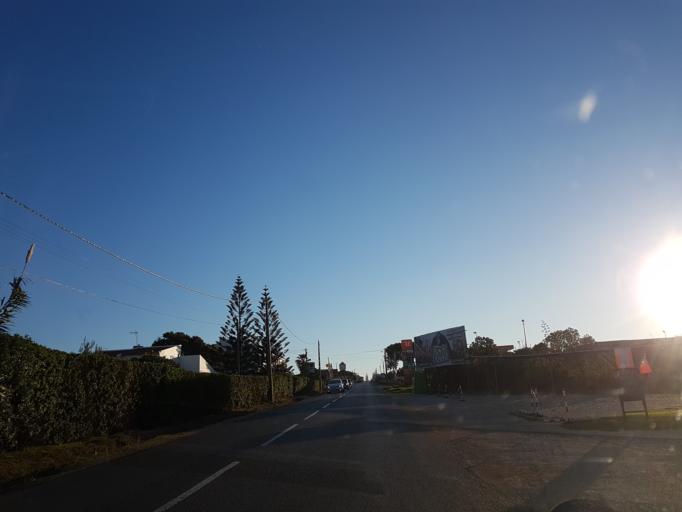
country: PT
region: Faro
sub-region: Vila do Bispo
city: Sagres
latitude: 37.0141
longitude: -8.9420
